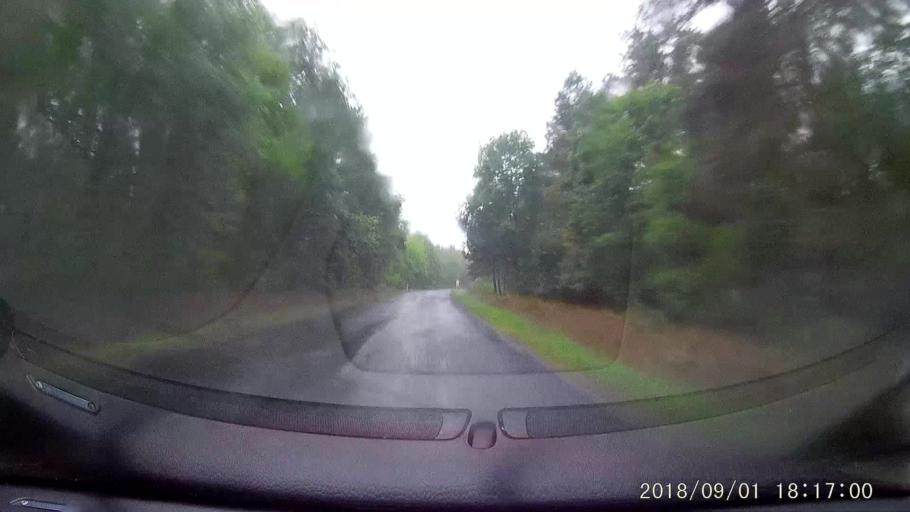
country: PL
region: Lower Silesian Voivodeship
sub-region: Powiat zgorzelecki
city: Piensk
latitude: 51.2665
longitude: 15.0515
